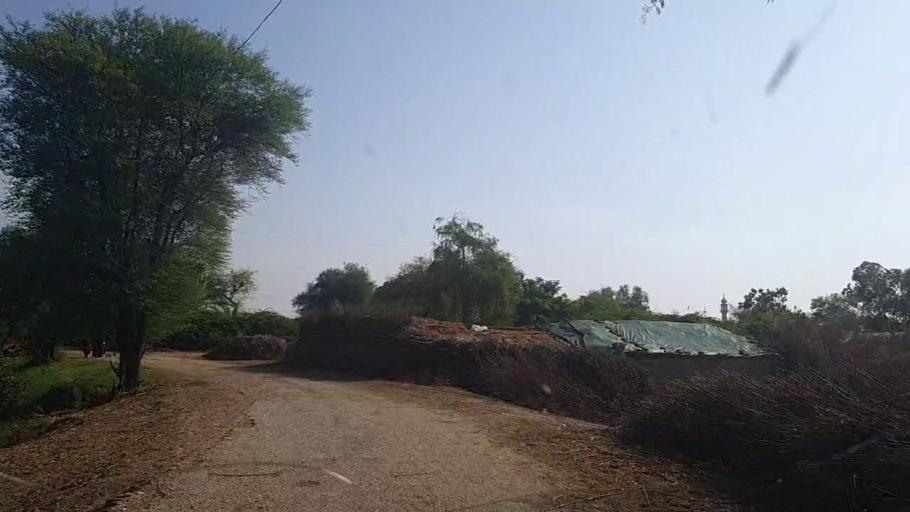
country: PK
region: Sindh
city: Khanpur
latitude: 27.7303
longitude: 69.3322
